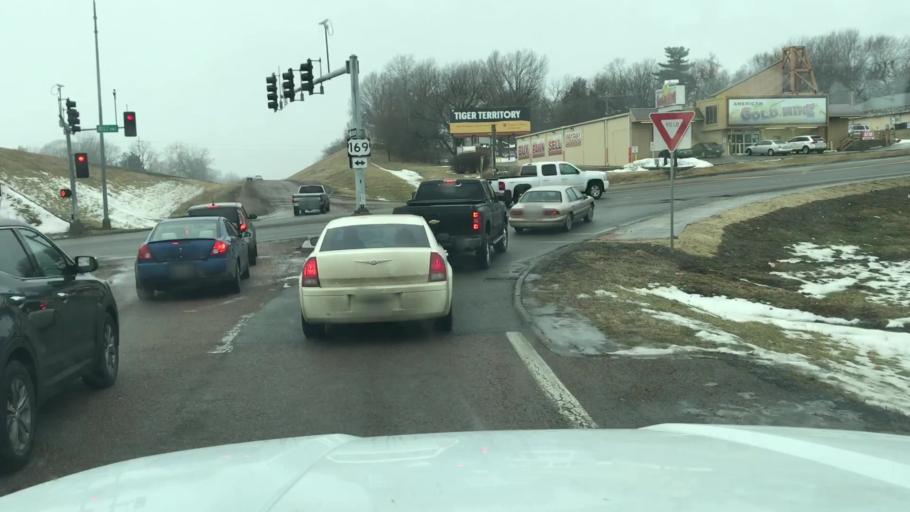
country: US
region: Missouri
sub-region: Buchanan County
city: Saint Joseph
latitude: 39.7473
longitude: -94.8017
